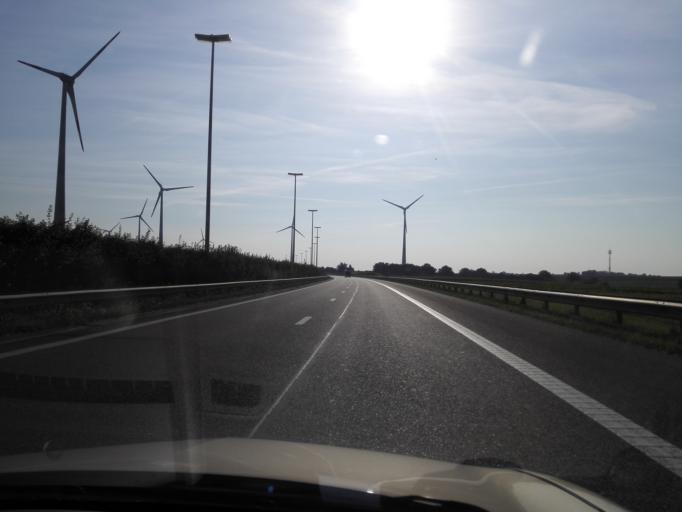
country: BE
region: Flanders
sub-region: Provincie Vlaams-Brabant
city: Kortenaken
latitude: 50.9434
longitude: 5.0306
